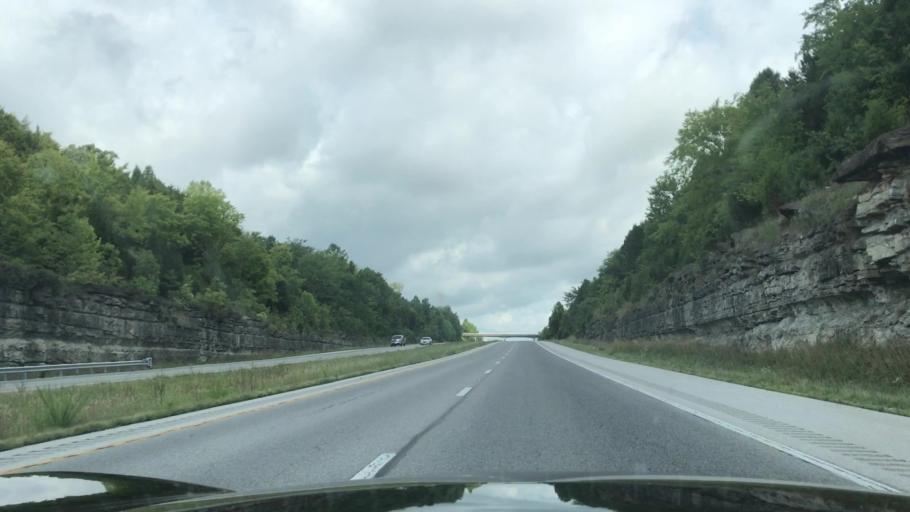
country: US
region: Kentucky
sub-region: Warren County
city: Bowling Green
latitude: 37.0237
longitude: -86.5301
